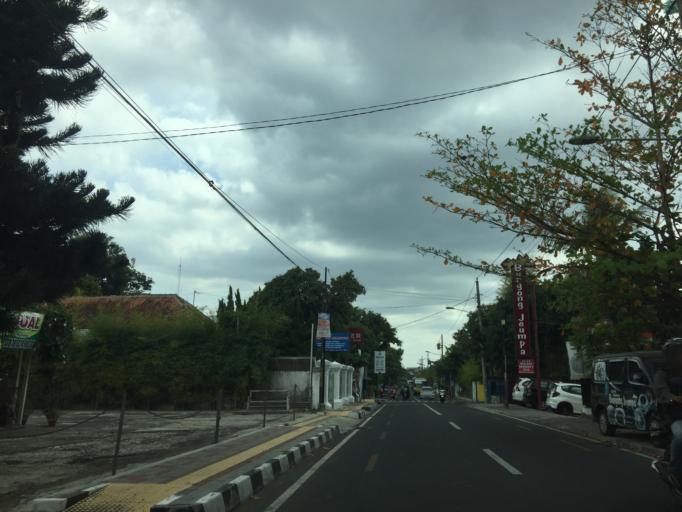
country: ID
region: Daerah Istimewa Yogyakarta
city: Yogyakarta
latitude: -7.7780
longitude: 110.3649
